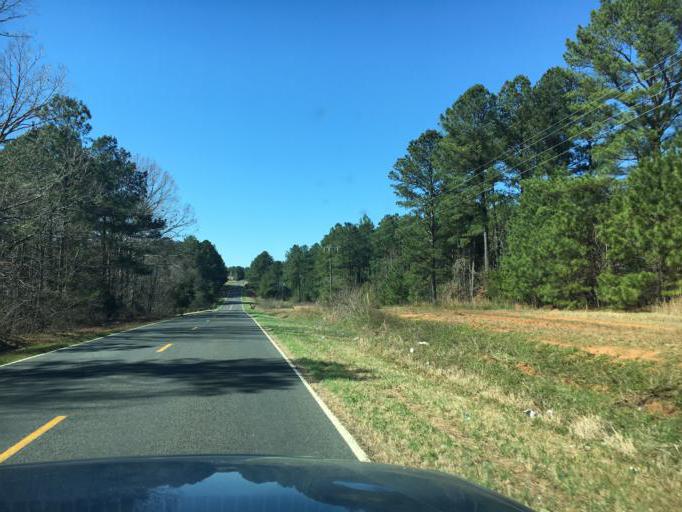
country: US
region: South Carolina
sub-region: Greenwood County
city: Ninety Six
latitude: 34.2917
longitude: -81.9665
